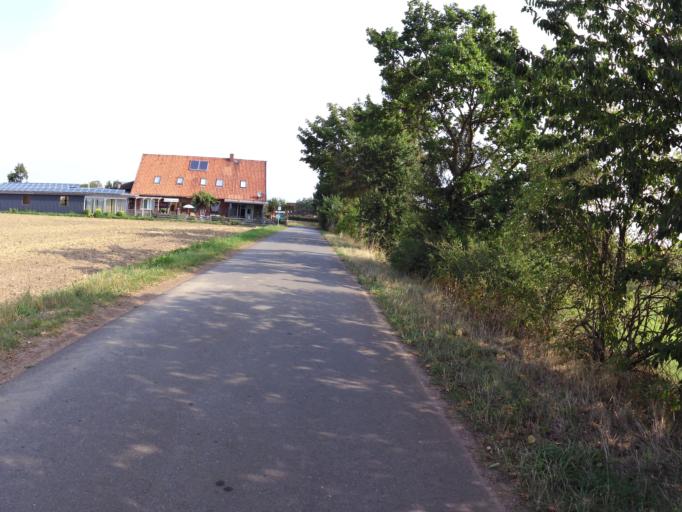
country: DE
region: Lower Saxony
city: Stolzenau
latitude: 52.4863
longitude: 9.0229
